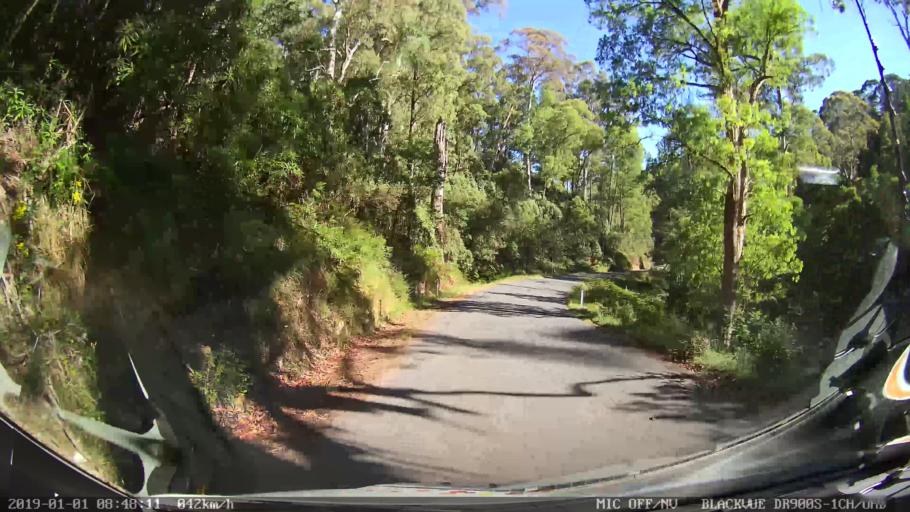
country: AU
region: New South Wales
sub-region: Snowy River
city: Jindabyne
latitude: -36.2903
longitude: 148.1992
